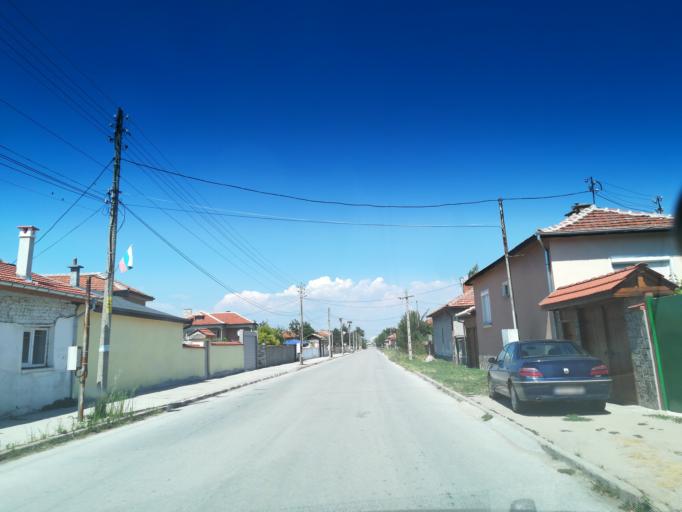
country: BG
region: Plovdiv
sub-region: Obshtina Sadovo
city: Sadovo
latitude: 42.0300
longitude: 25.1143
